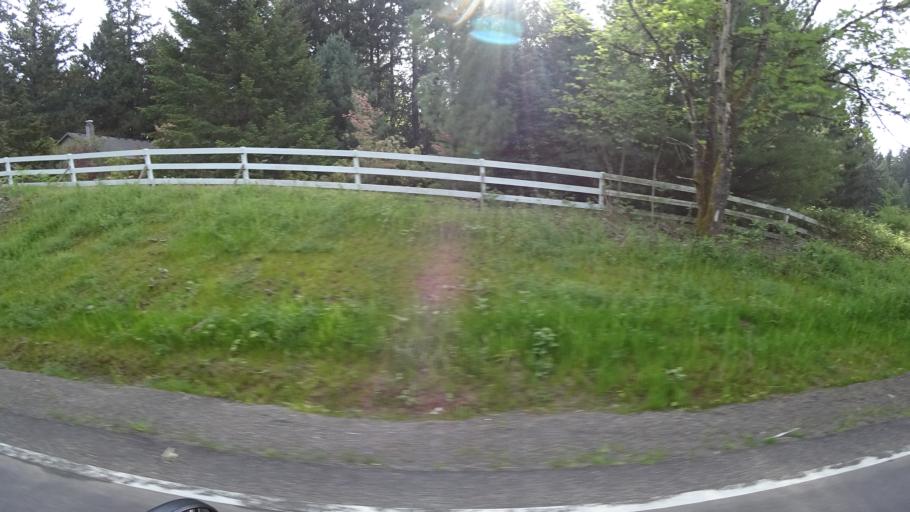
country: US
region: Oregon
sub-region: Washington County
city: Aloha
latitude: 45.4459
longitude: -122.8568
